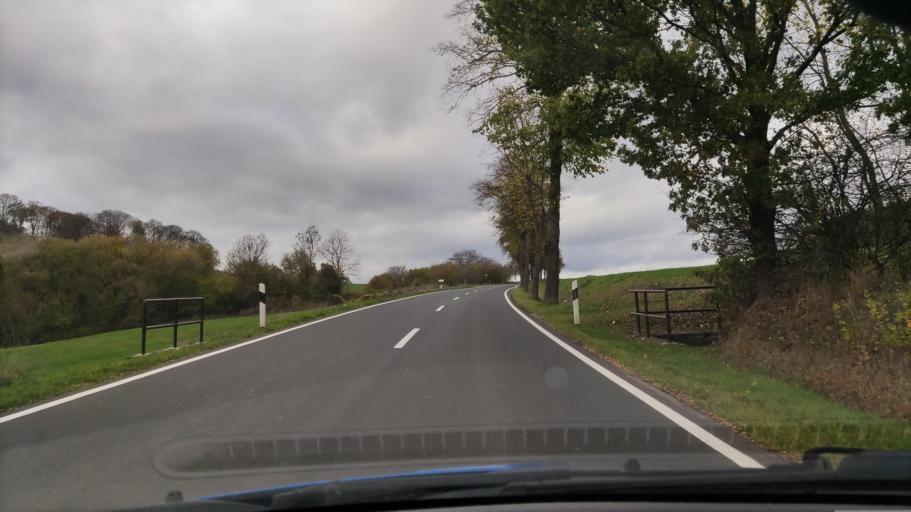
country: DE
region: Lower Saxony
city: Wangelnstedt
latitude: 51.8647
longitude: 9.7077
